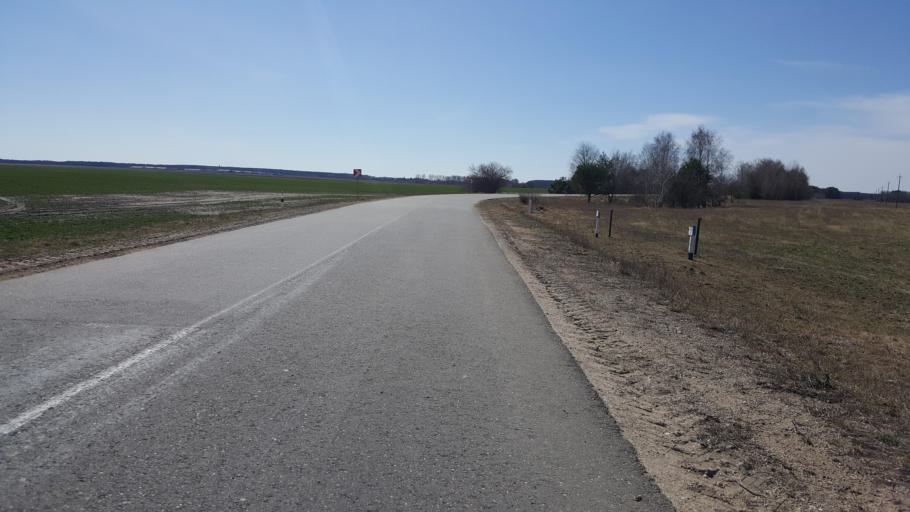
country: BY
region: Brest
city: Kamyanyets
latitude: 52.3100
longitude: 23.8889
